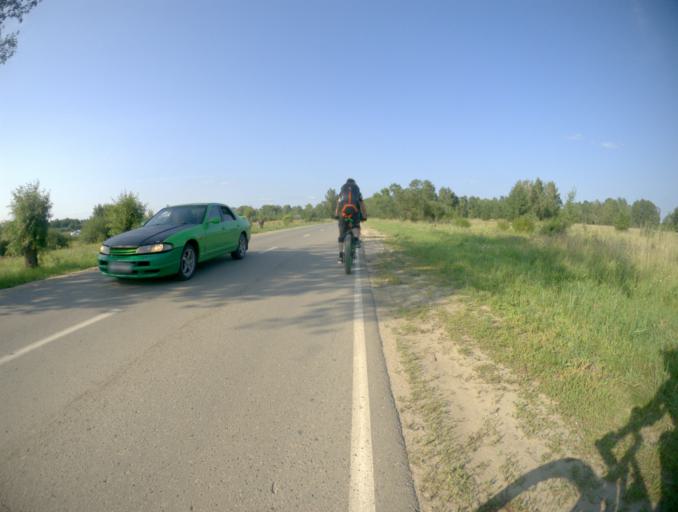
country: RU
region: Nizjnij Novgorod
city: Bor
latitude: 56.3476
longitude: 44.0501
